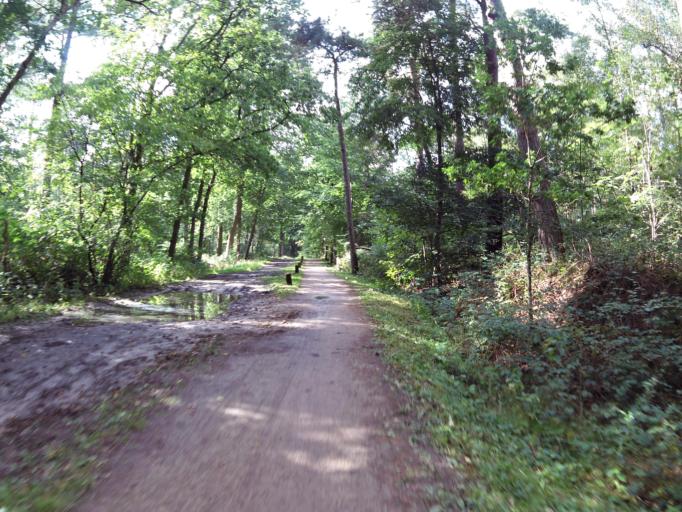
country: NL
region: North Holland
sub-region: Gemeente Hilversum
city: Hilversum
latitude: 52.1739
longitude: 5.2059
